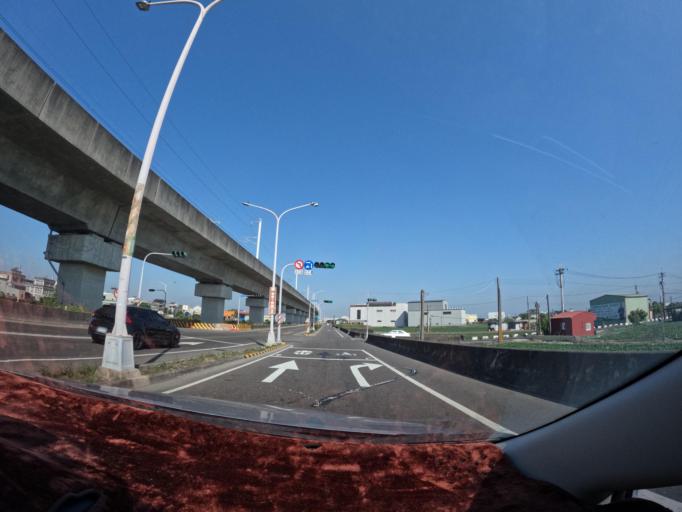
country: TW
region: Taiwan
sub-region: Tainan
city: Tainan
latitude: 23.0192
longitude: 120.2892
